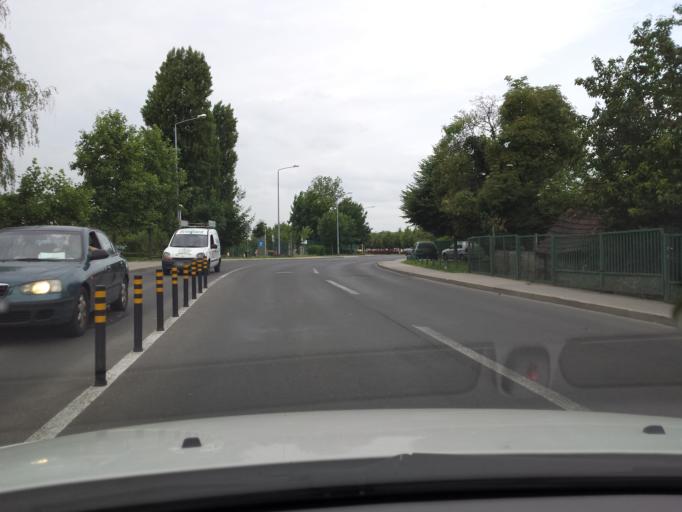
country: HR
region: Grad Zagreb
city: Zagreb - Centar
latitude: 45.8042
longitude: 15.9467
